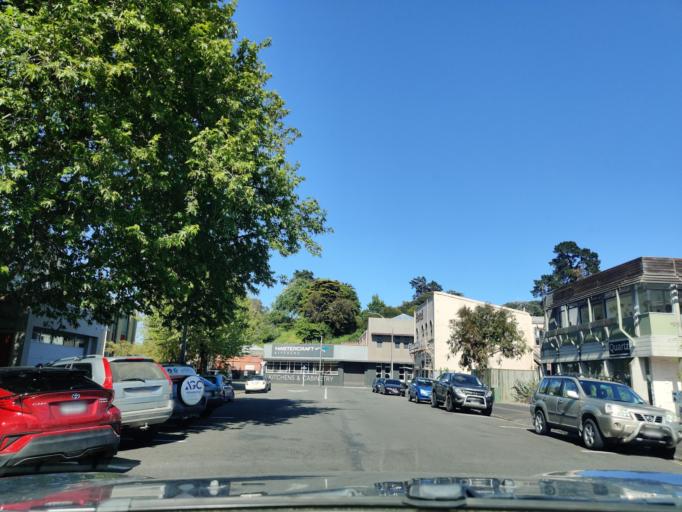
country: NZ
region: Manawatu-Wanganui
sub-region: Wanganui District
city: Wanganui
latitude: -39.9312
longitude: 175.0564
